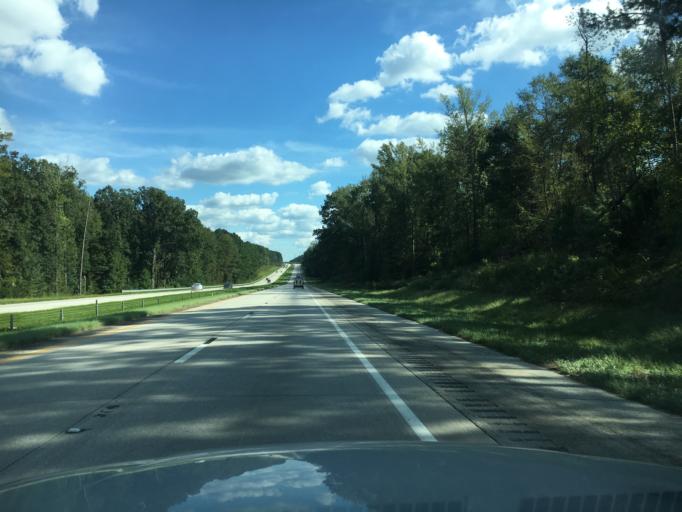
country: US
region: South Carolina
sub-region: Laurens County
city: Laurens
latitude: 34.5943
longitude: -82.0549
